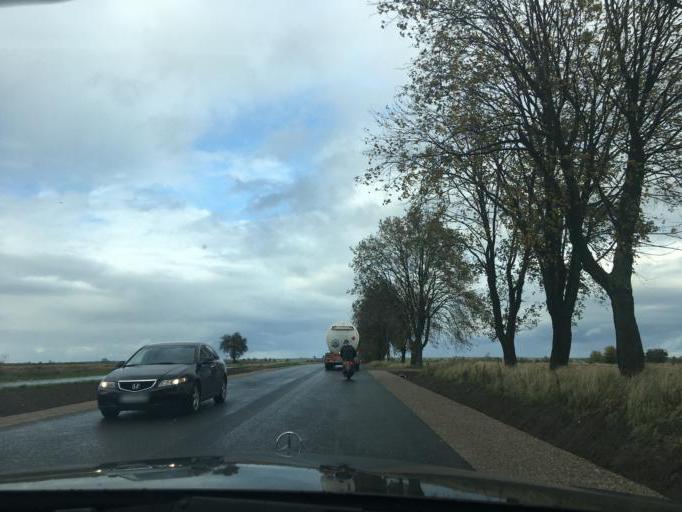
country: PL
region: Lublin Voivodeship
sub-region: Powiat lubelski
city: Wysokie
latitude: 50.9424
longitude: 22.6749
